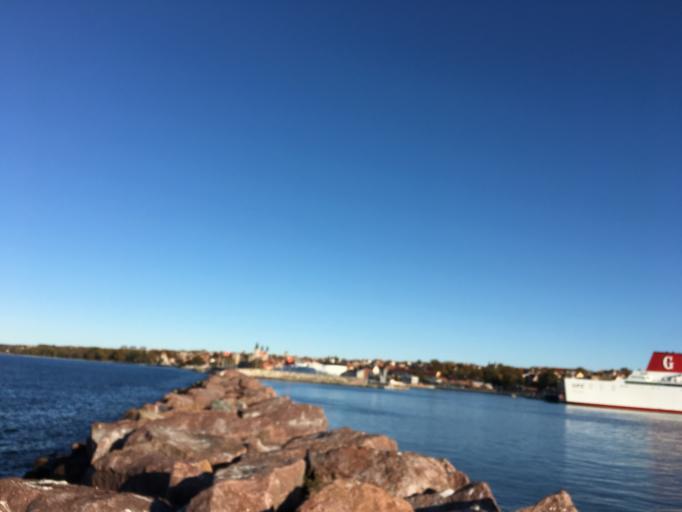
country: SE
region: Gotland
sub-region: Gotland
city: Visby
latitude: 57.6369
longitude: 18.2735
